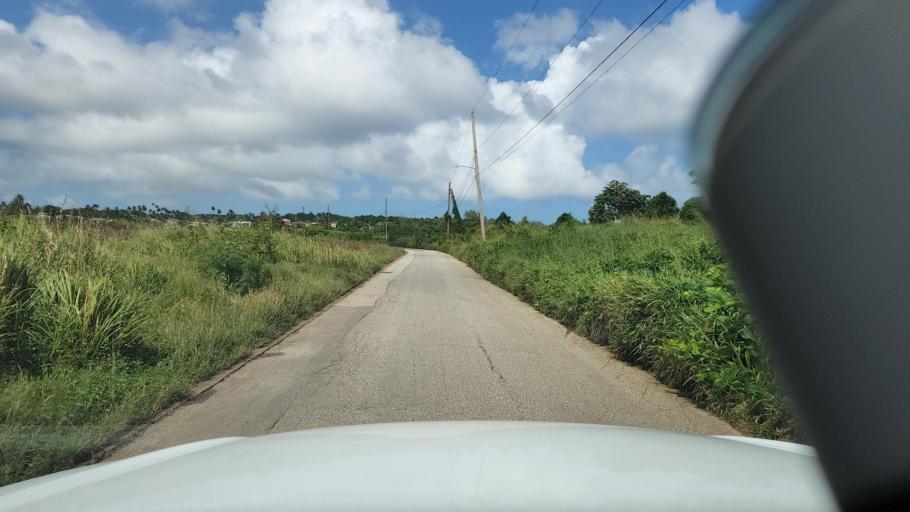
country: BB
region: Saint John
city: Four Cross Roads
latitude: 13.1900
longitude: -59.5067
